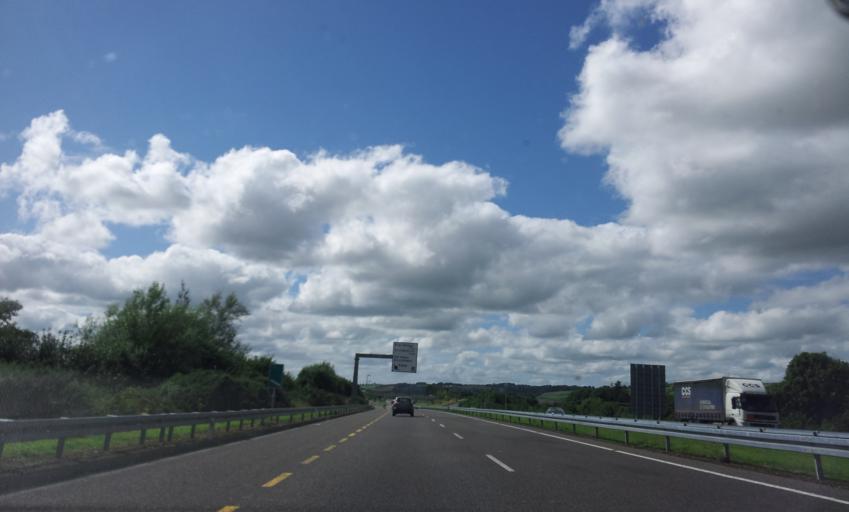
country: IE
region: Munster
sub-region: County Cork
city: Killumney
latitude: 51.8784
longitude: -8.6268
